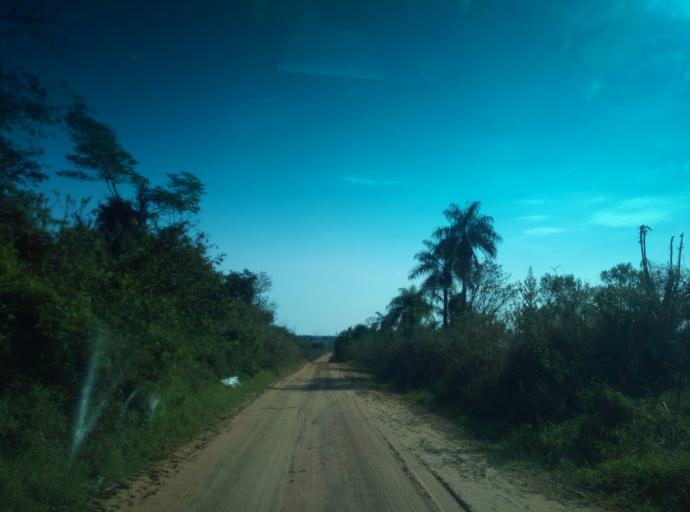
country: PY
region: Caaguazu
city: Doctor Cecilio Baez
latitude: -25.1649
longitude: -56.2163
